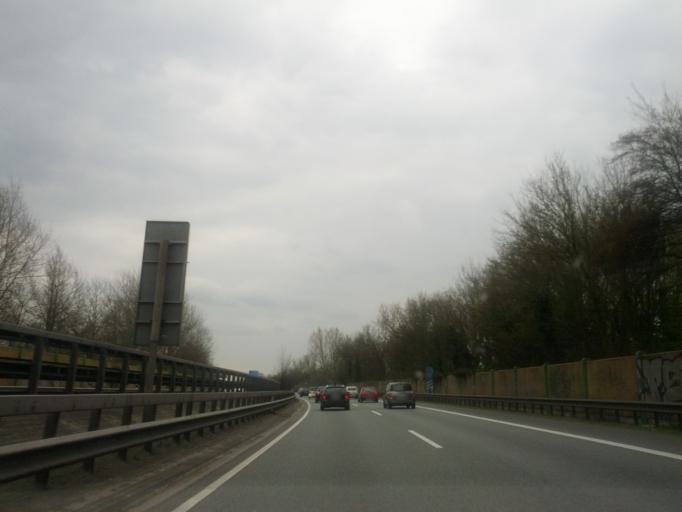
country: DE
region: Lower Saxony
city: Oldenburg
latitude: 53.1412
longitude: 8.1902
